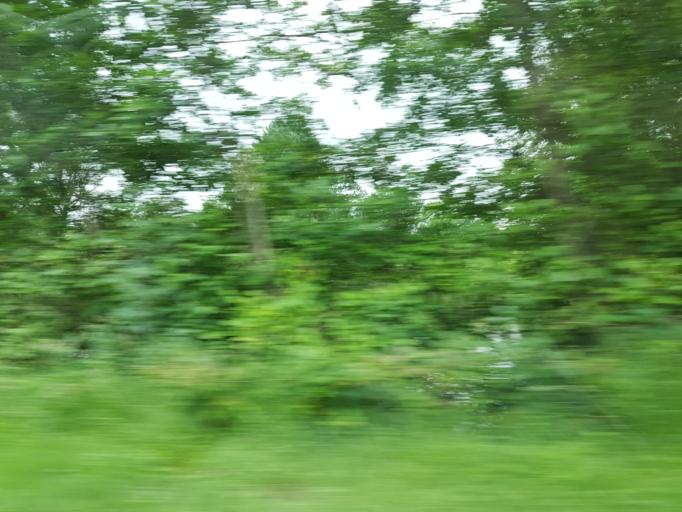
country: FR
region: Bourgogne
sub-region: Departement de la Nievre
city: Lormes
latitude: 47.1647
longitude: 3.8394
